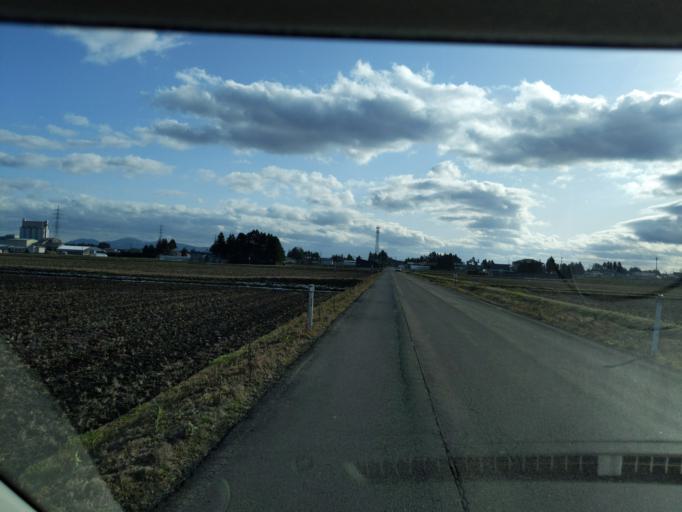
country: JP
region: Iwate
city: Mizusawa
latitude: 39.1446
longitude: 141.0790
